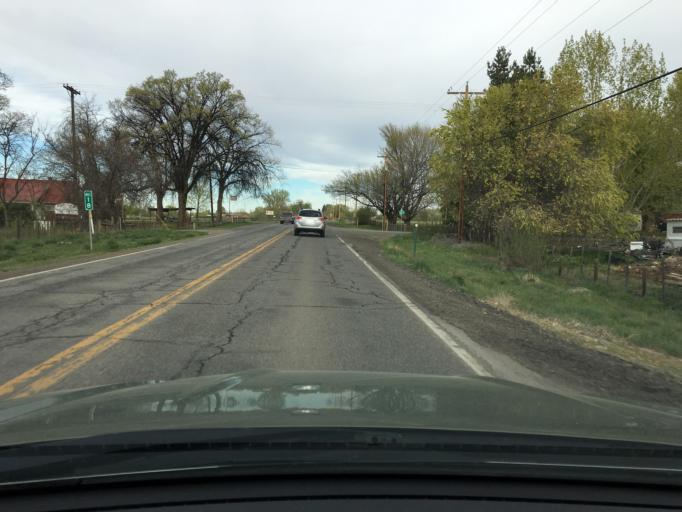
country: US
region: Colorado
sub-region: Delta County
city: Paonia
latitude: 38.8000
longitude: -107.7623
